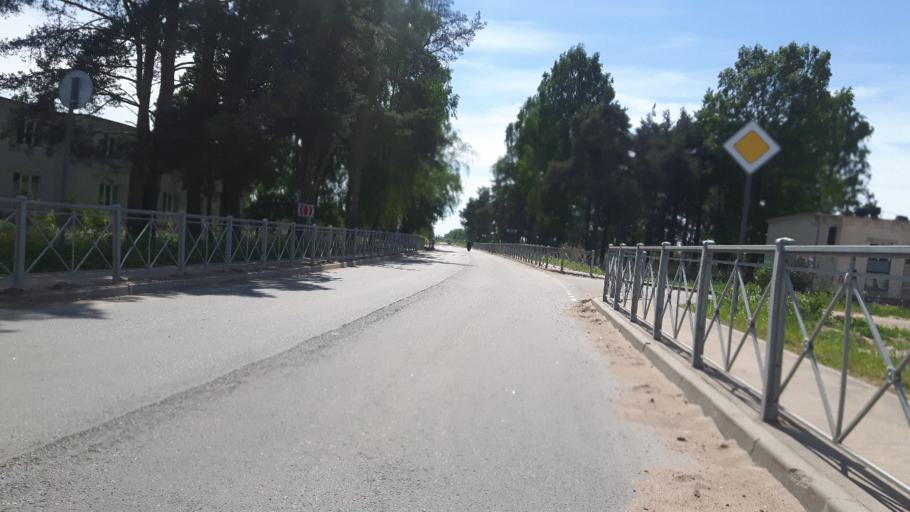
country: RU
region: Leningrad
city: Ust'-Luga
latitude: 59.5789
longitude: 28.1767
